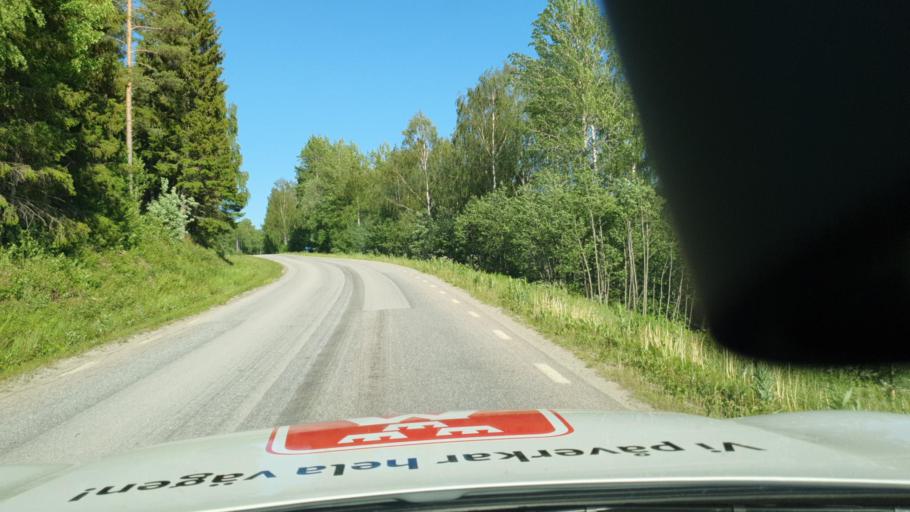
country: SE
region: Vaesterbotten
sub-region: Vannas Kommun
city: Vaennaes
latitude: 63.8676
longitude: 19.6603
